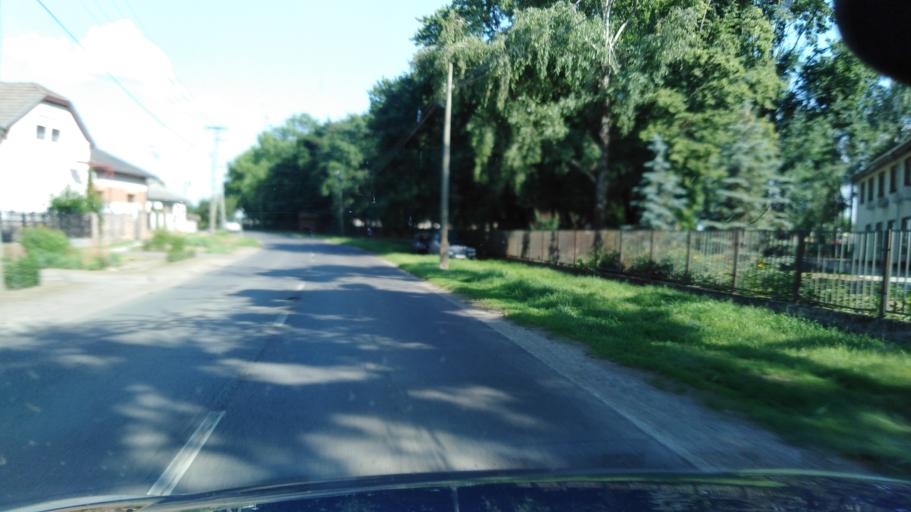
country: HU
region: Szabolcs-Szatmar-Bereg
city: Nyirbator
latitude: 47.8262
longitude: 22.1447
